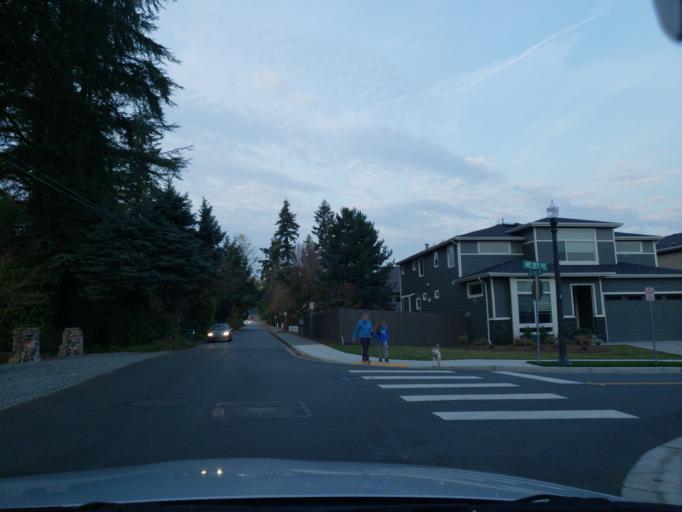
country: US
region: Washington
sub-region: King County
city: Bothell
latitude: 47.7563
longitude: -122.2235
